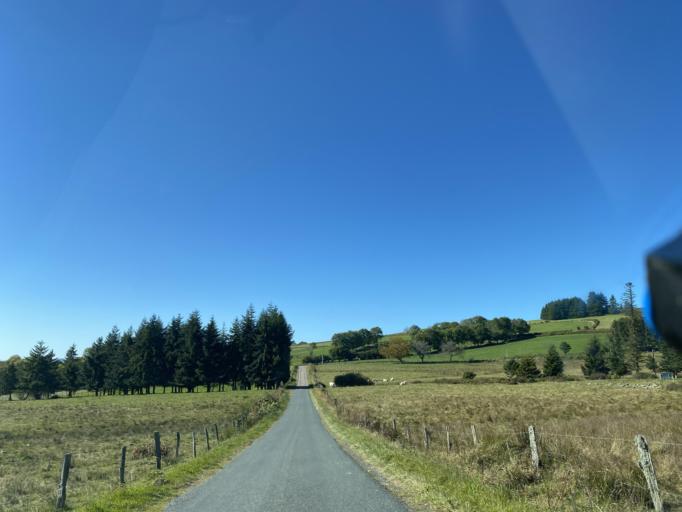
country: FR
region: Rhone-Alpes
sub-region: Departement de la Loire
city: Saint-Just-en-Chevalet
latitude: 45.9617
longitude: 3.8718
